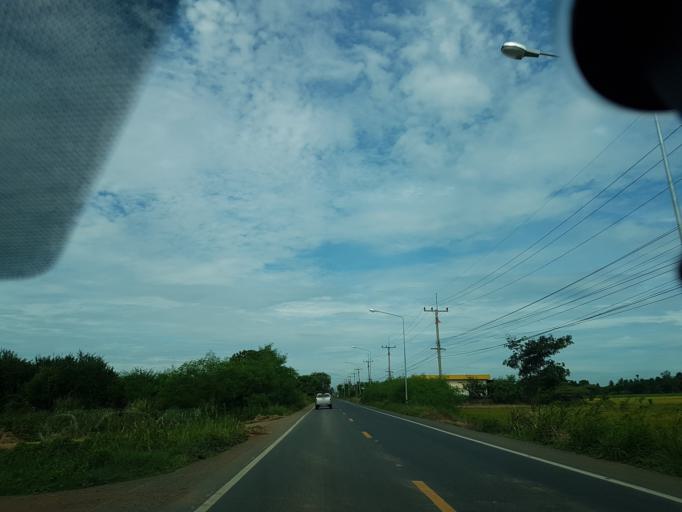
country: TH
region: Lop Buri
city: Tha Wung
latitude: 14.7361
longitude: 100.5220
